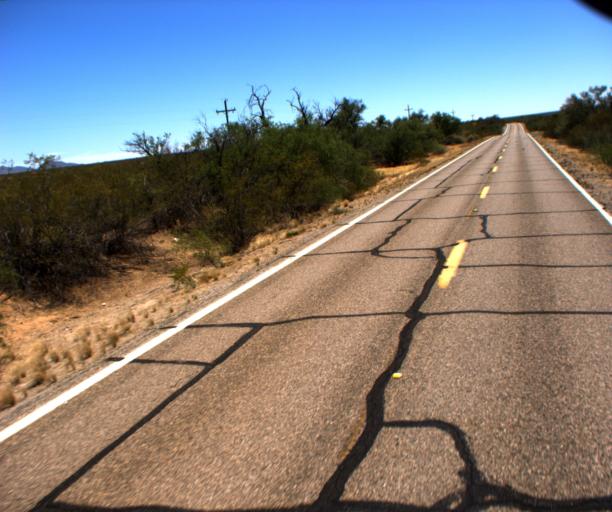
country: US
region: Arizona
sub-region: Pima County
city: Three Points
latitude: 31.9617
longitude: -111.3861
